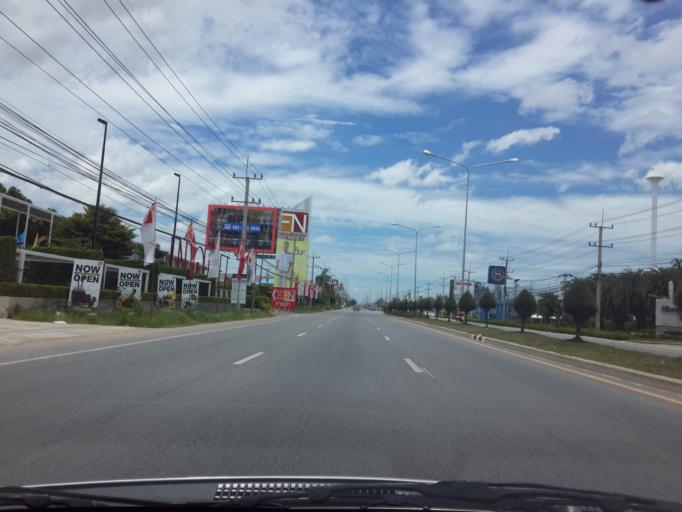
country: TH
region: Prachuap Khiri Khan
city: Hua Hin
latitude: 12.6652
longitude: 99.9523
